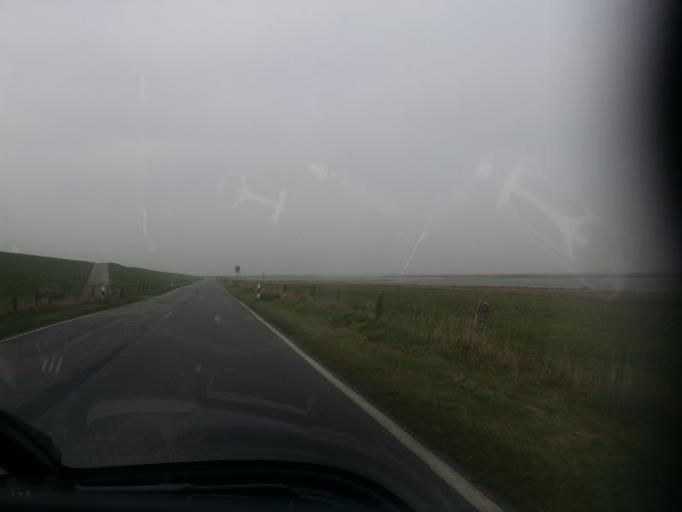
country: DE
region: Schleswig-Holstein
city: Ockholm
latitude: 54.6627
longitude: 8.7977
